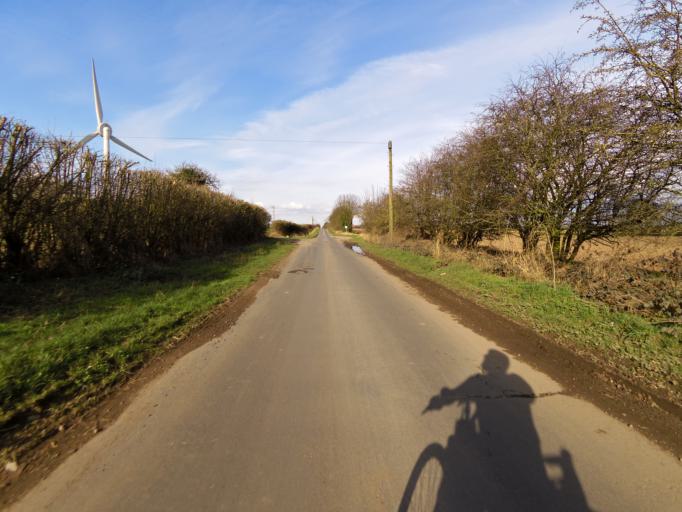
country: GB
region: England
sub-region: East Riding of Yorkshire
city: Pollington
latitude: 53.6830
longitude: -1.0661
